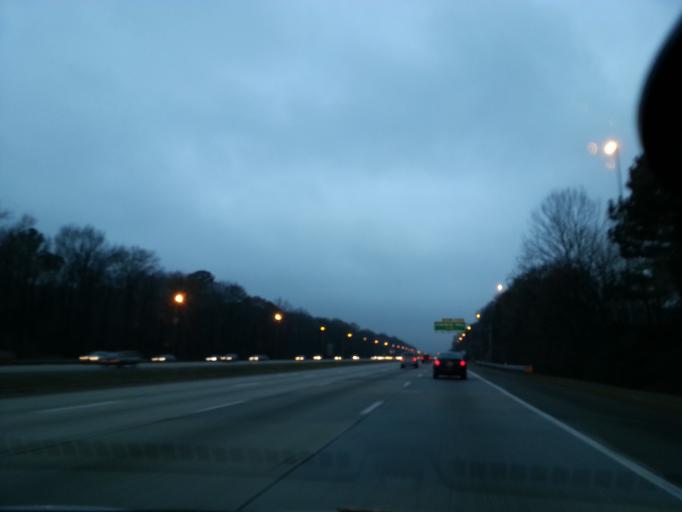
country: US
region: Virginia
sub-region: City of Chesapeake
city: Chesapeake
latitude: 36.7982
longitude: -76.2054
